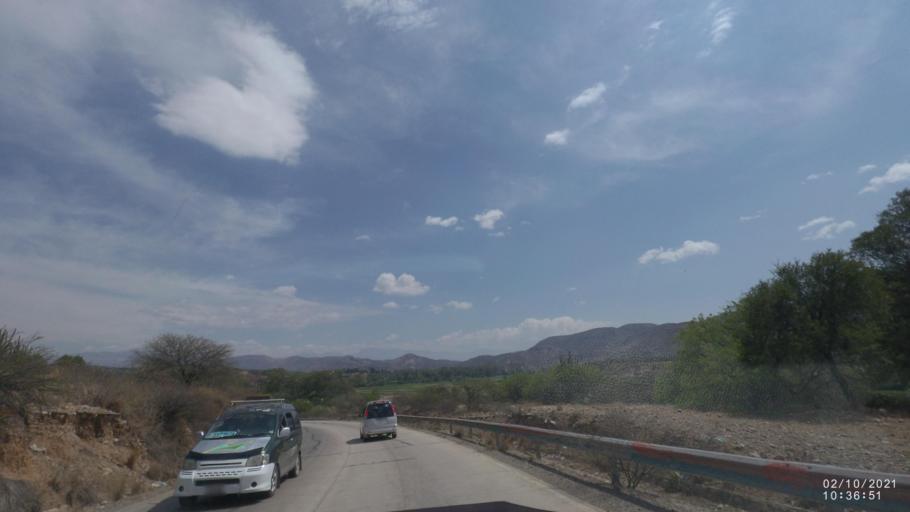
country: BO
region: Cochabamba
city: Capinota
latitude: -17.6460
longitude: -66.2590
